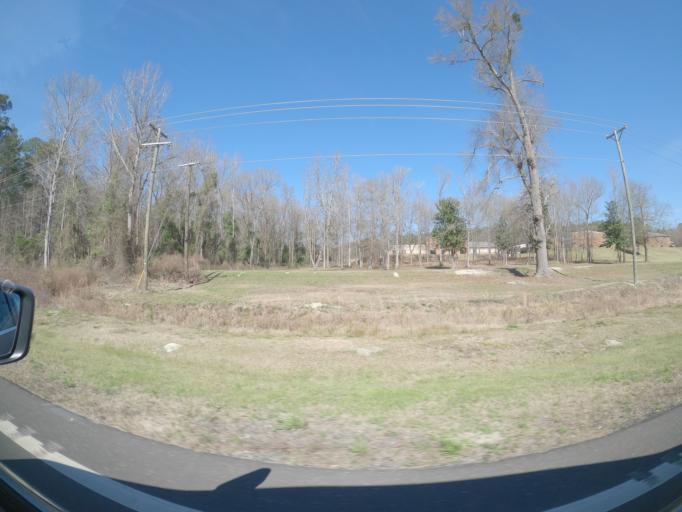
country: US
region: South Carolina
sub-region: Aiken County
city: Clearwater
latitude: 33.5097
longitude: -81.8737
